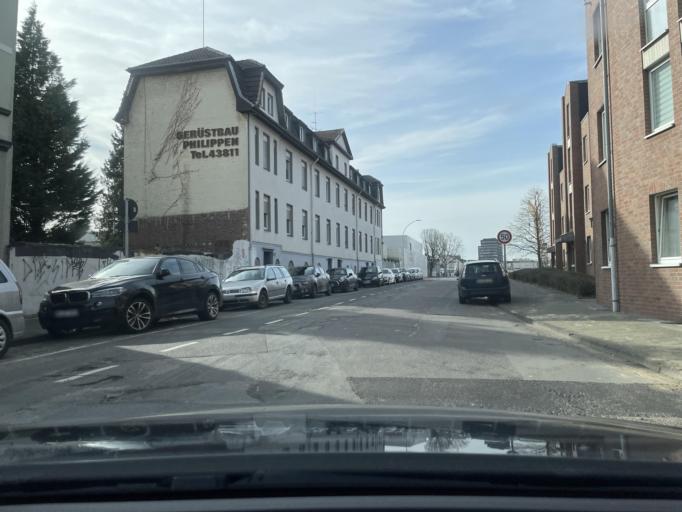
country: DE
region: North Rhine-Westphalia
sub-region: Regierungsbezirk Dusseldorf
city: Monchengladbach
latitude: 51.1982
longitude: 6.4577
